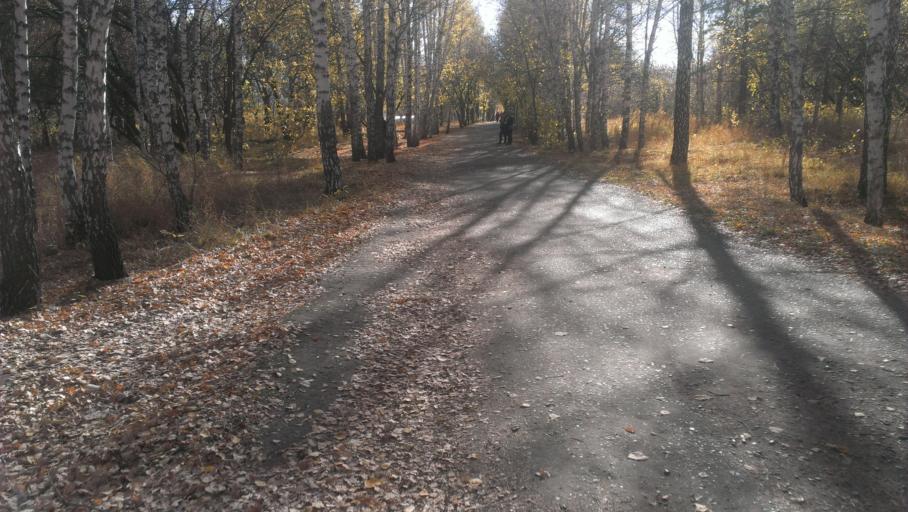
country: RU
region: Altai Krai
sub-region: Gorod Barnaulskiy
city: Barnaul
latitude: 53.3600
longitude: 83.6851
